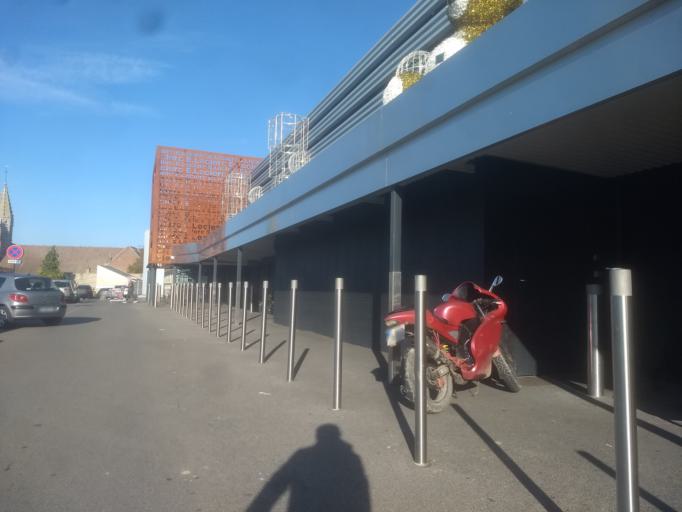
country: FR
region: Nord-Pas-de-Calais
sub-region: Departement du Pas-de-Calais
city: Arras
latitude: 50.2809
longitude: 2.7821
